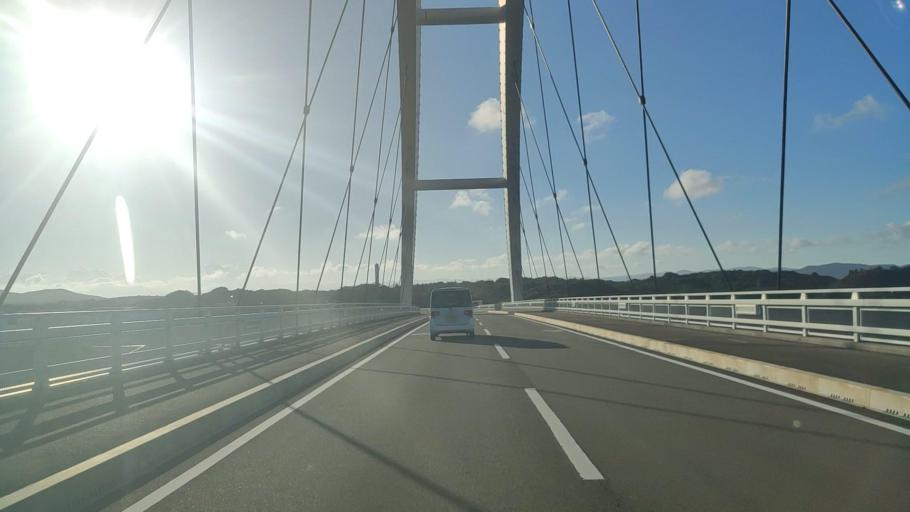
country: JP
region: Mie
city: Toba
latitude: 34.2657
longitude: 136.8141
